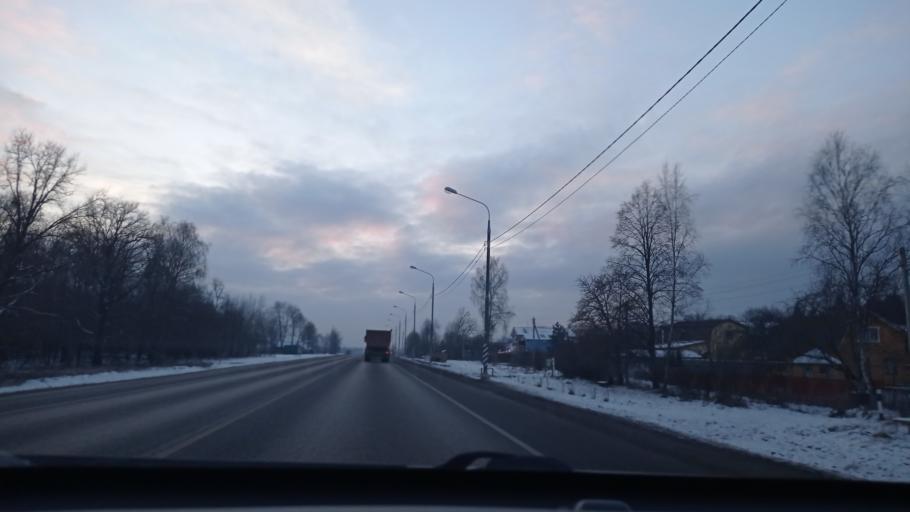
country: RU
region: Kaluga
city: Zhukovo
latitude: 55.1514
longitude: 36.8164
